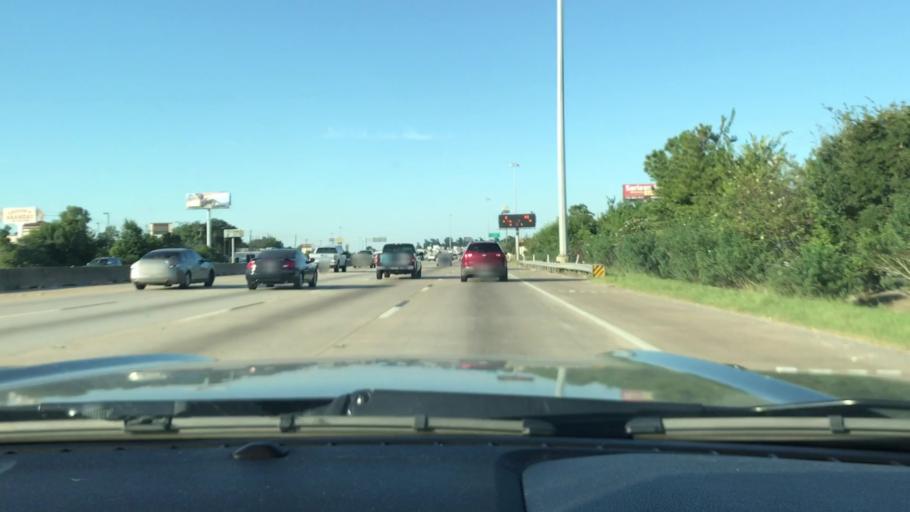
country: US
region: Texas
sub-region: Harris County
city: Aldine
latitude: 29.8964
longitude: -95.3147
